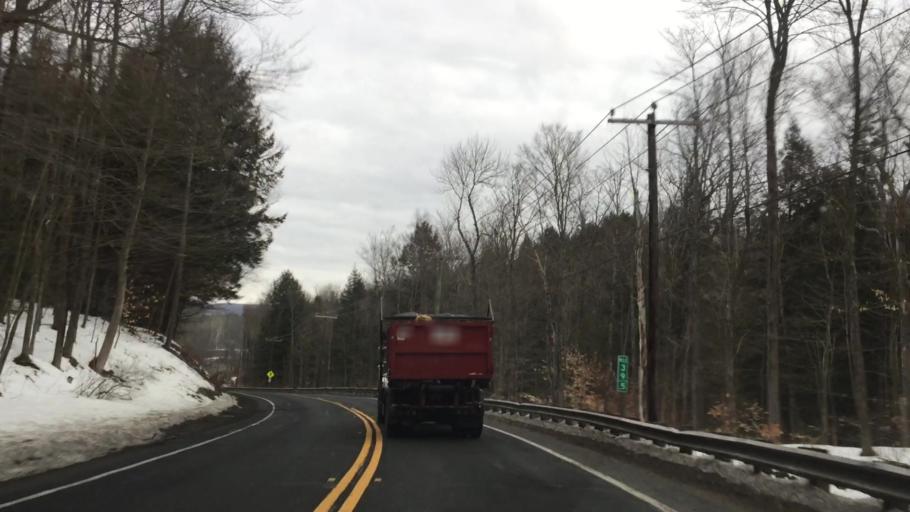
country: US
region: Massachusetts
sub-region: Berkshire County
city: Hinsdale
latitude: 42.4551
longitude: -73.1289
